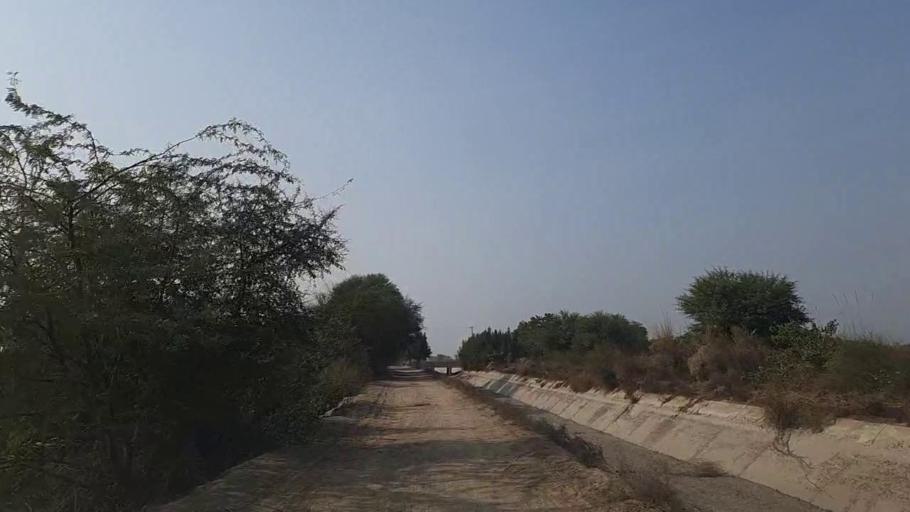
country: PK
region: Sindh
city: Daur
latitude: 26.5137
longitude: 68.4448
